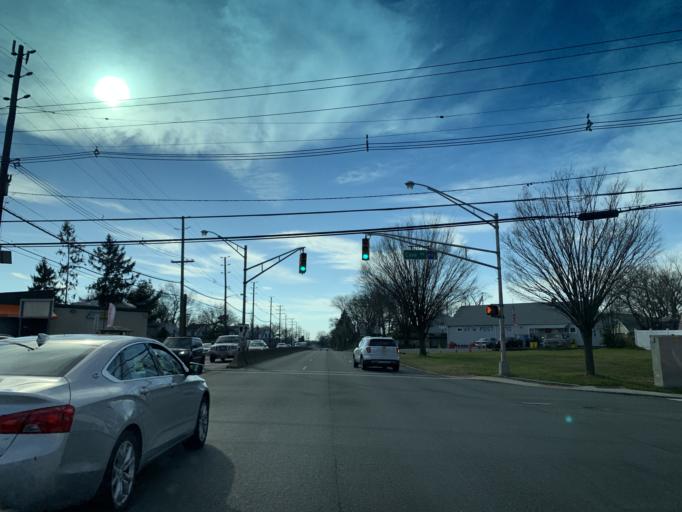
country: US
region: New Jersey
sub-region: Camden County
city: Pennsauken
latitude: 39.9616
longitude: -75.0521
